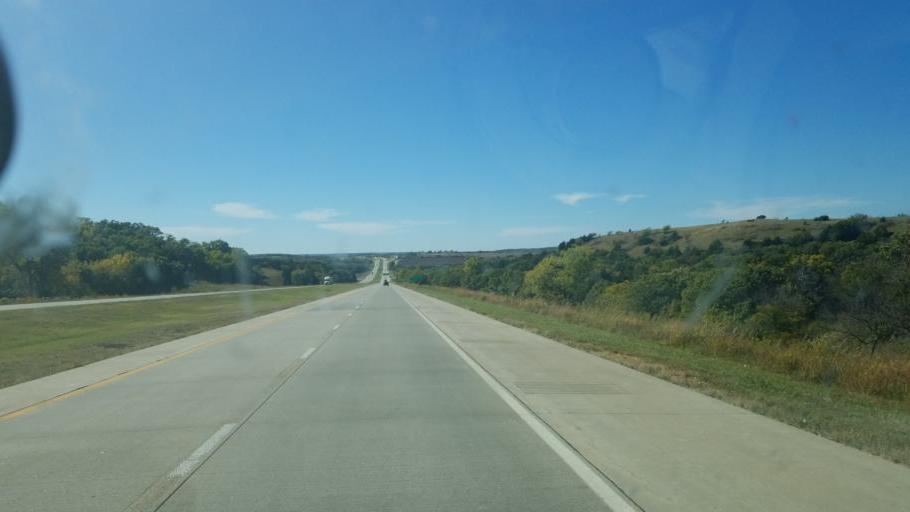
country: US
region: Kansas
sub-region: Riley County
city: Ogden
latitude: 39.0635
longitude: -96.7077
